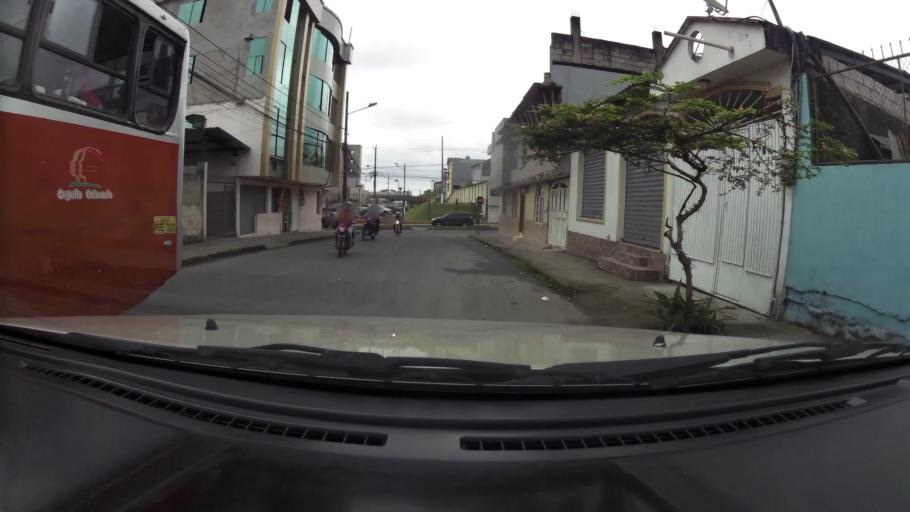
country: EC
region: Santo Domingo de los Tsachilas
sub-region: Canton Santo Domingo de los Colorados
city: Santo Domingo de los Colorados
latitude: -0.2540
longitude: -79.1523
